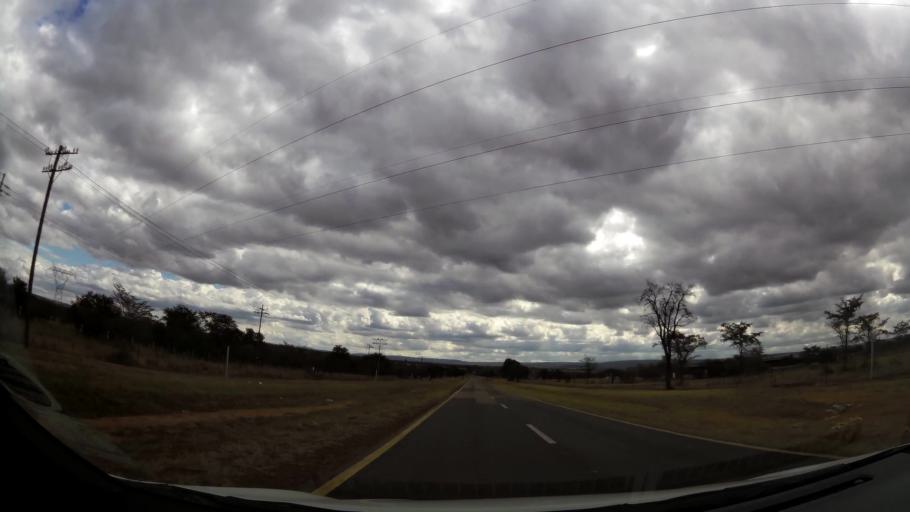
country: ZA
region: Limpopo
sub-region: Waterberg District Municipality
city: Modimolle
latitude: -24.7585
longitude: 28.4542
